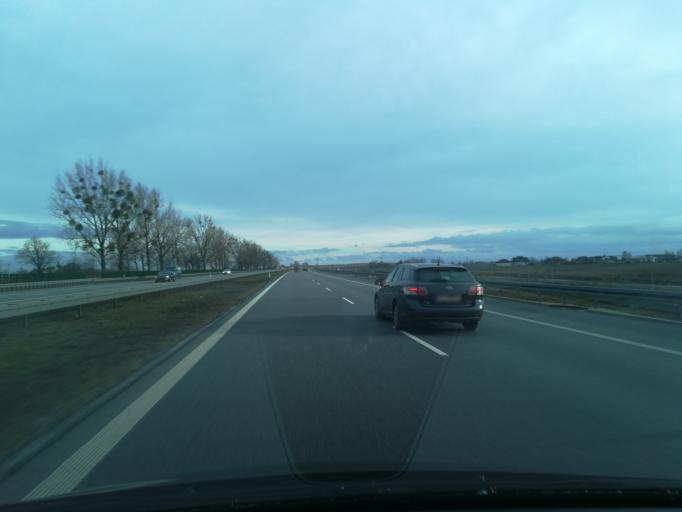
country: PL
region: Kujawsko-Pomorskie
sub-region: Powiat aleksandrowski
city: Raciazek
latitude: 52.8370
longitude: 18.7965
